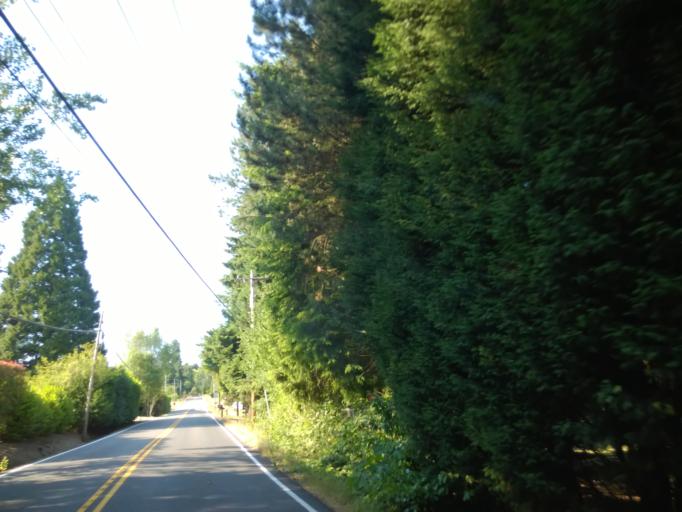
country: US
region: Washington
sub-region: King County
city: Woodinville
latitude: 47.7770
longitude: -122.1694
